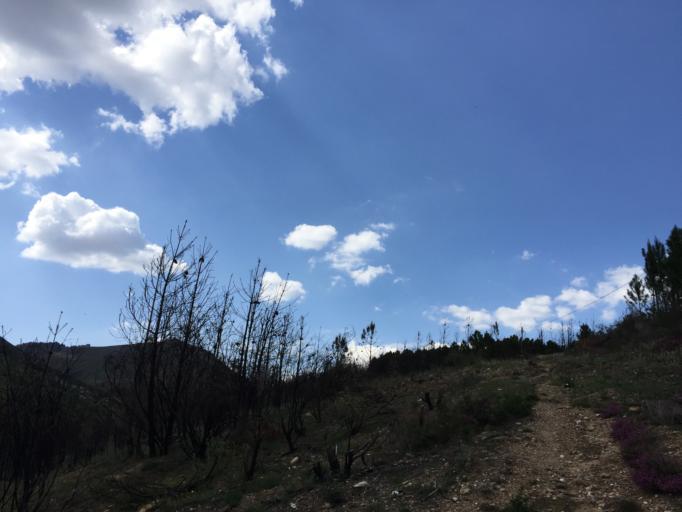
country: PT
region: Coimbra
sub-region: Pampilhosa da Serra
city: Pampilhosa da Serra
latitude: 40.1024
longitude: -7.8661
